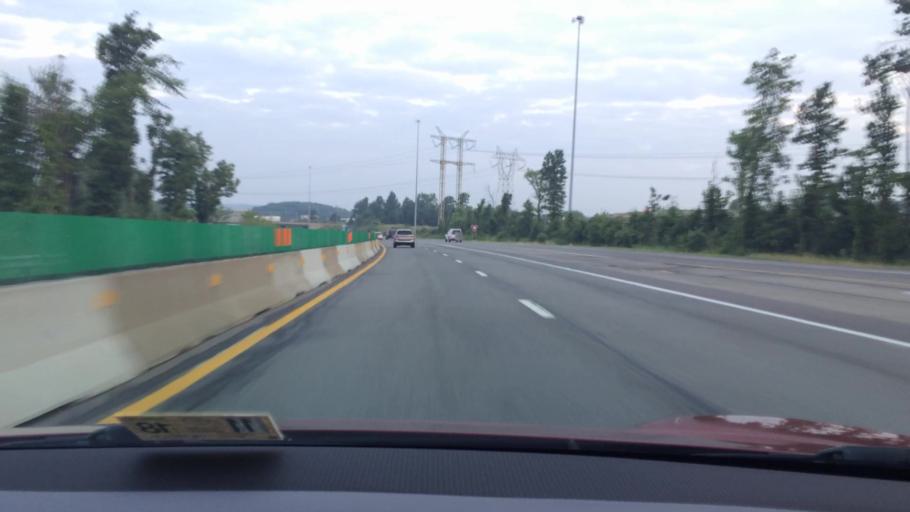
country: US
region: Ohio
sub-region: Summit County
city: Richfield
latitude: 41.2713
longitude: -81.6227
